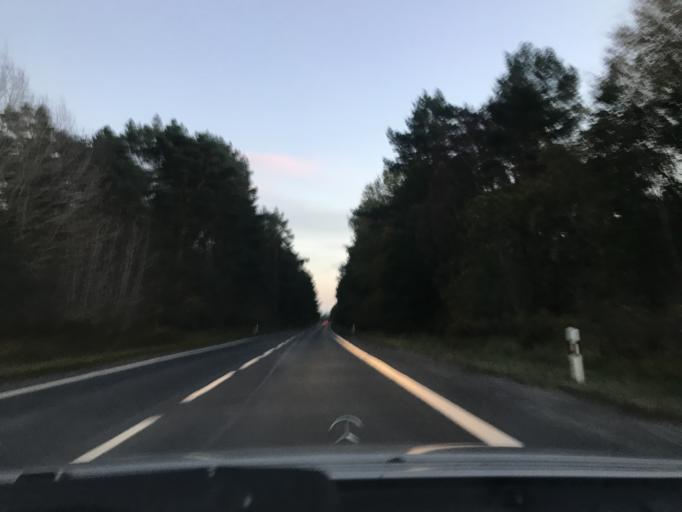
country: DE
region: Mecklenburg-Vorpommern
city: Karlshagen
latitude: 54.1254
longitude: 13.8243
